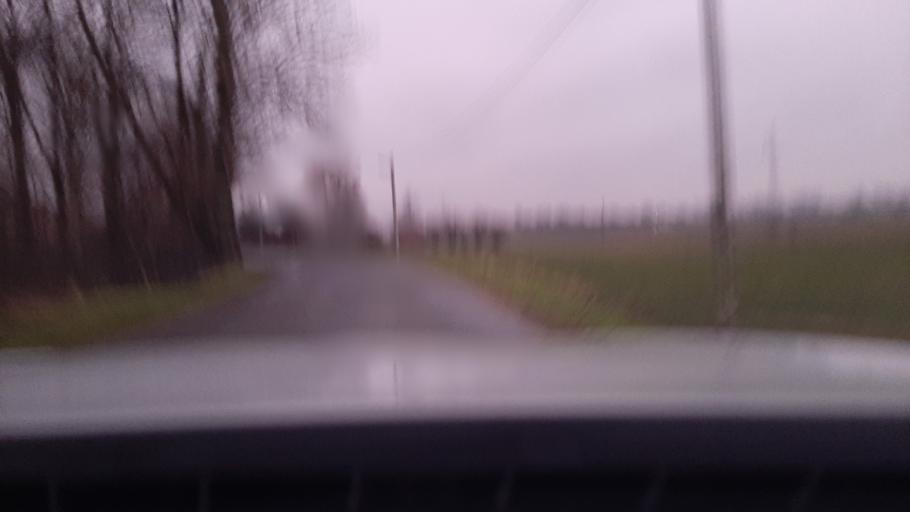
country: PL
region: Lublin Voivodeship
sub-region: Powiat lubelski
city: Garbow
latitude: 51.3527
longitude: 22.3857
